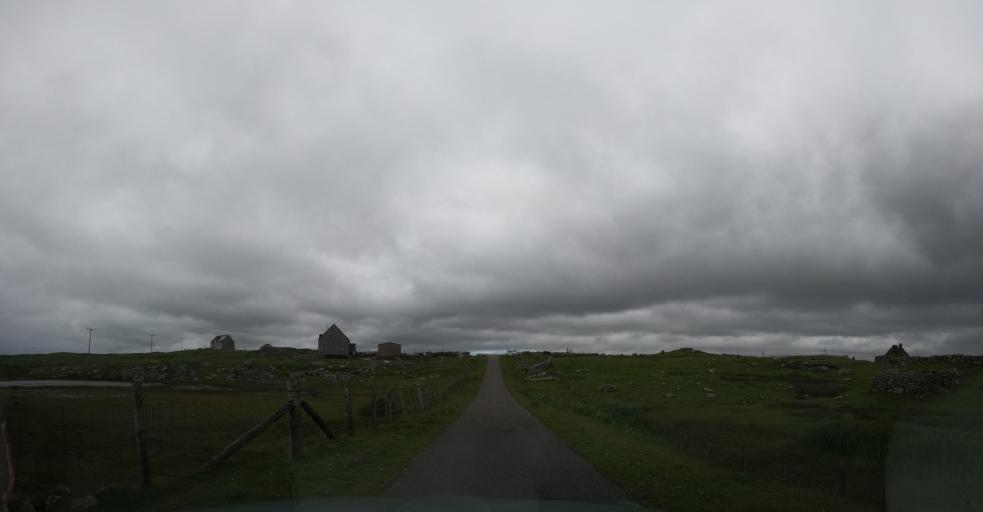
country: GB
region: Scotland
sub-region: Eilean Siar
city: Isle of North Uist
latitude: 57.5458
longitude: -7.3445
